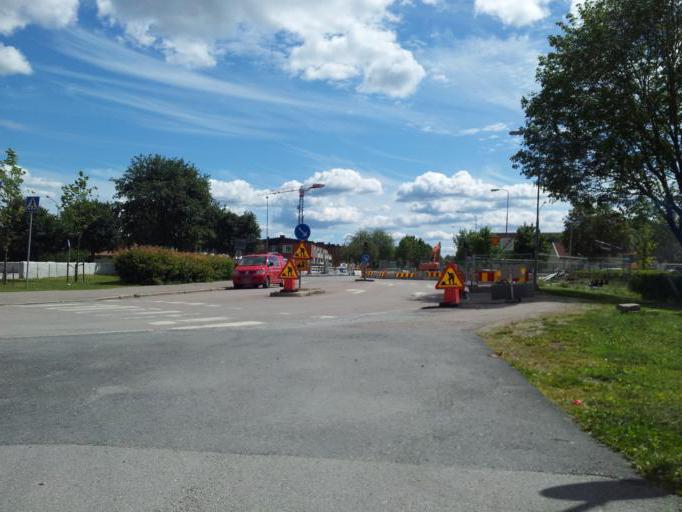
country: SE
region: Uppsala
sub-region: Uppsala Kommun
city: Uppsala
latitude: 59.8689
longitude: 17.6431
